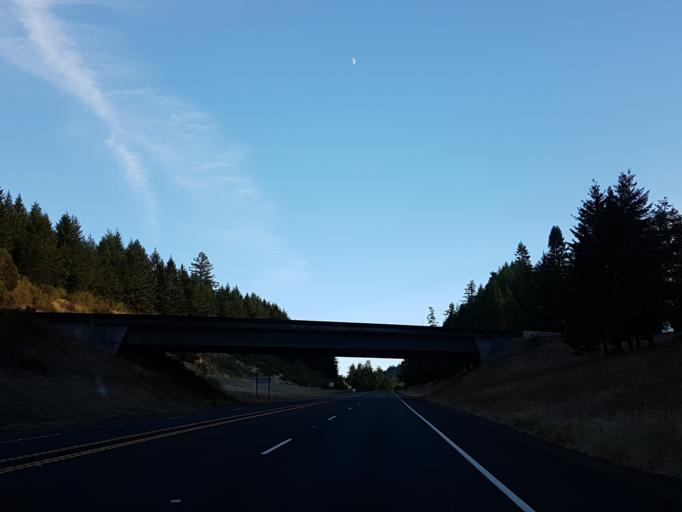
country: US
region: California
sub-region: Humboldt County
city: Redway
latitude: 39.9449
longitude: -123.7797
